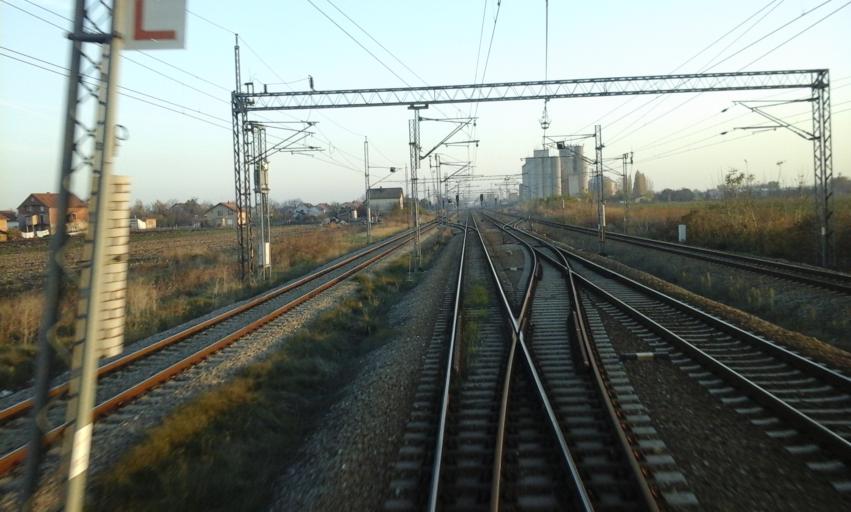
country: RS
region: Autonomna Pokrajina Vojvodina
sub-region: Sremski Okrug
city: Stara Pazova
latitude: 44.9928
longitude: 20.1330
